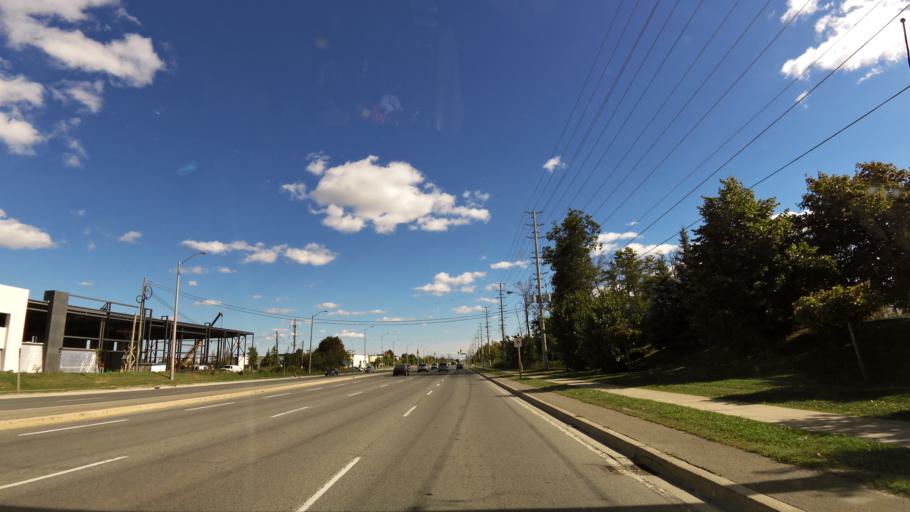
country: CA
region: Ontario
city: Brampton
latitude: 43.7504
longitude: -79.6811
